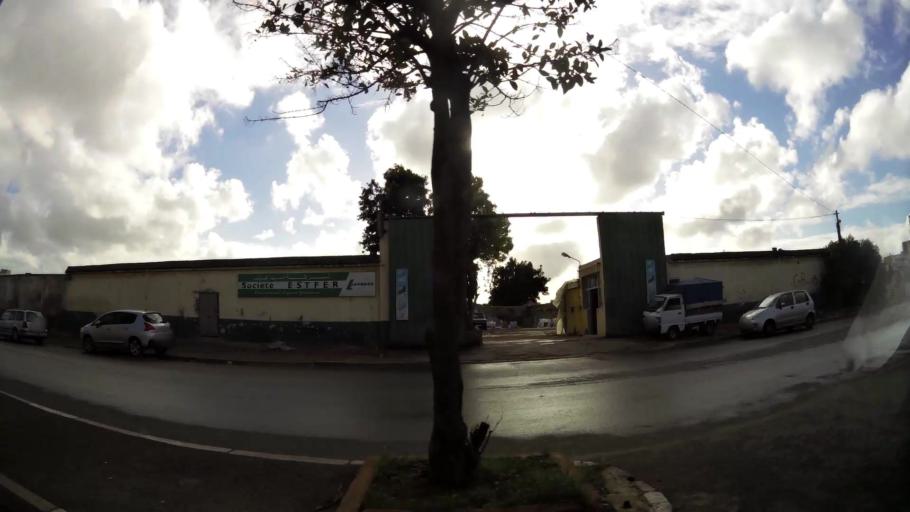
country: MA
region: Grand Casablanca
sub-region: Casablanca
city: Casablanca
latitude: 33.5454
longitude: -7.5892
